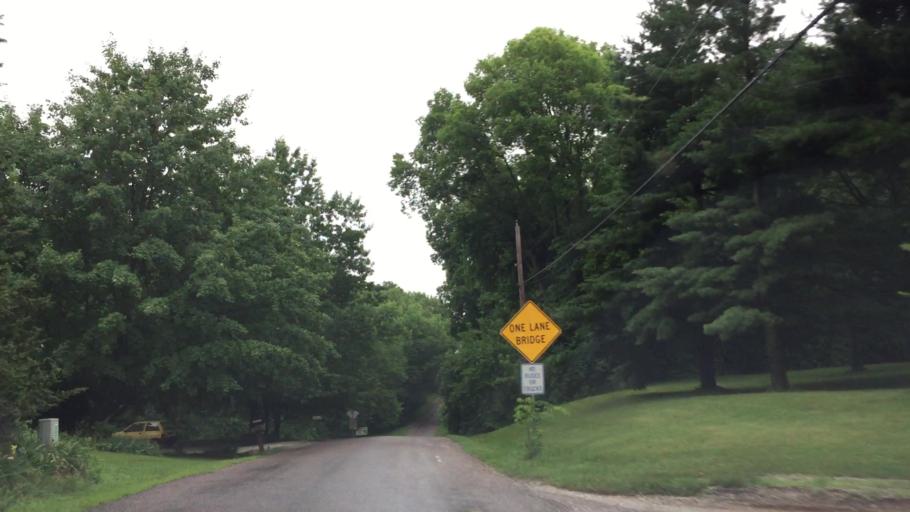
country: US
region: Illinois
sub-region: Hancock County
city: Nauvoo
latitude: 40.5376
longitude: -91.3760
